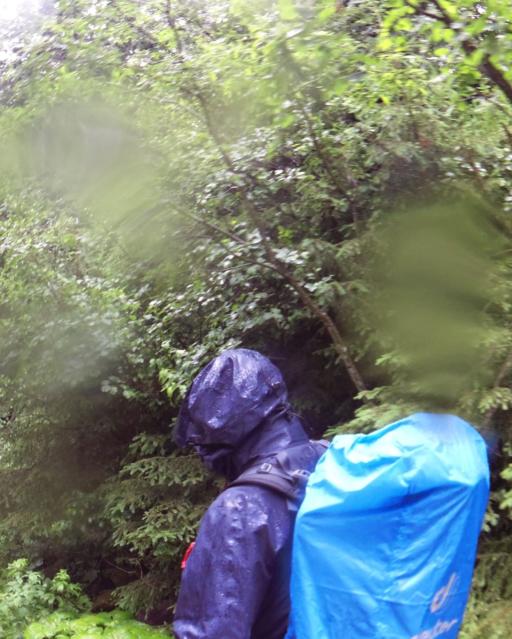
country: AT
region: Tyrol
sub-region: Politischer Bezirk Innsbruck Land
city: Neustift im Stubaital
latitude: 47.0207
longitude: 11.2231
